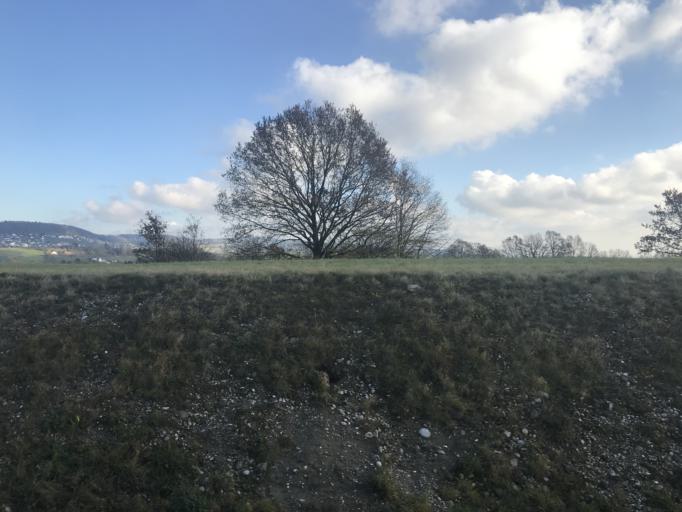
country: CH
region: Zurich
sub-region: Bezirk Andelfingen
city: Dachsen
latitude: 47.6660
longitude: 8.5979
